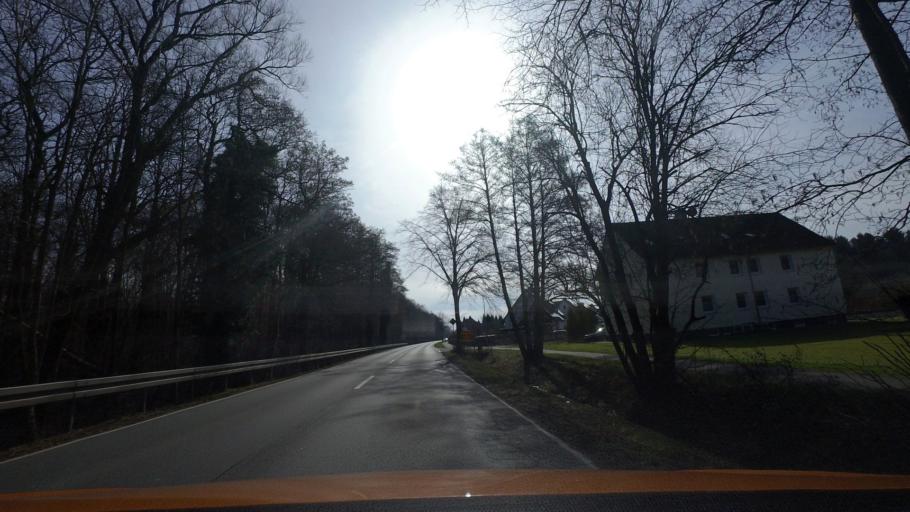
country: DE
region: Lower Saxony
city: Niedernwohren
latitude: 52.3695
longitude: 9.1311
